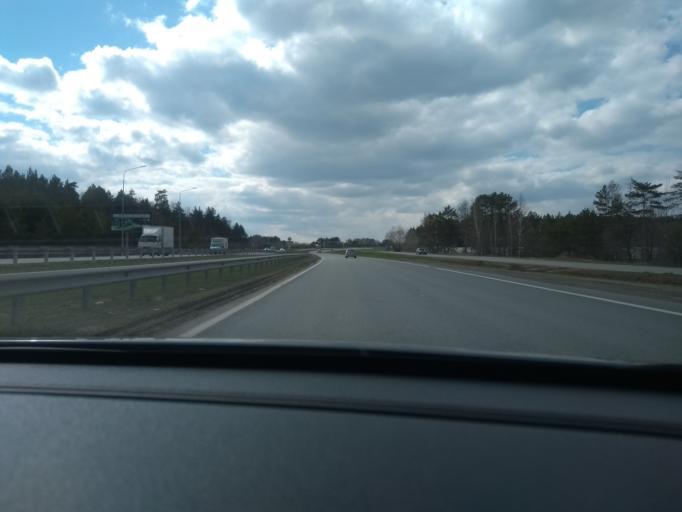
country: RU
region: Tatarstan
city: Yelabuga
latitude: 55.7816
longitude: 52.1878
